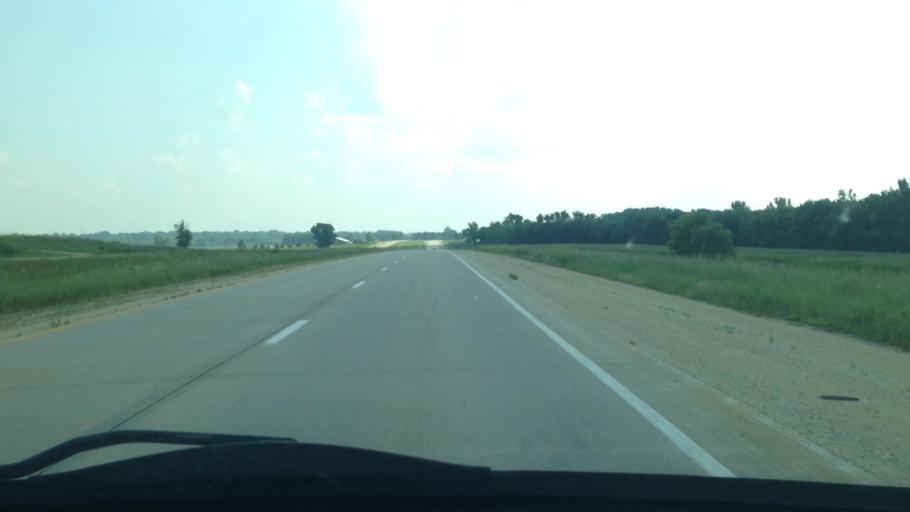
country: US
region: Iowa
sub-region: Bremer County
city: Denver
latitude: 42.6945
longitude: -92.3377
